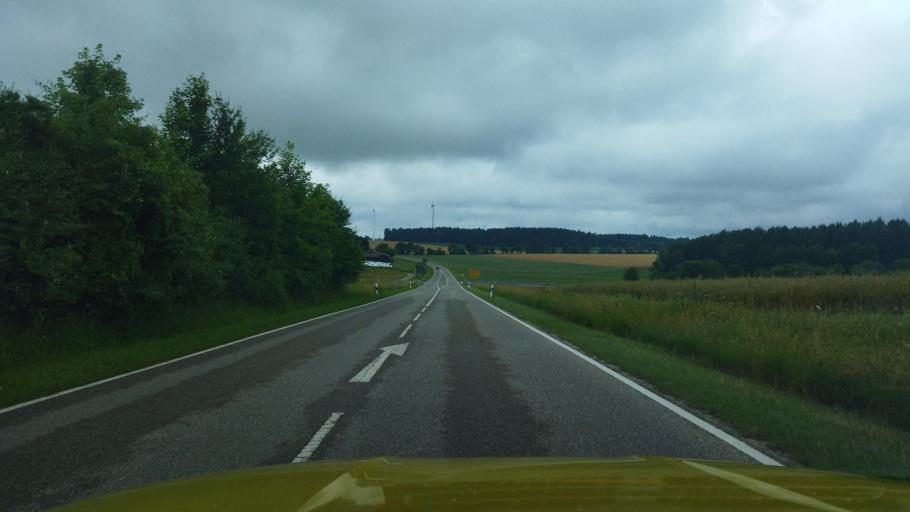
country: DE
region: Bavaria
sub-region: Upper Bavaria
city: Denkendorf
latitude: 48.9469
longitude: 11.5401
